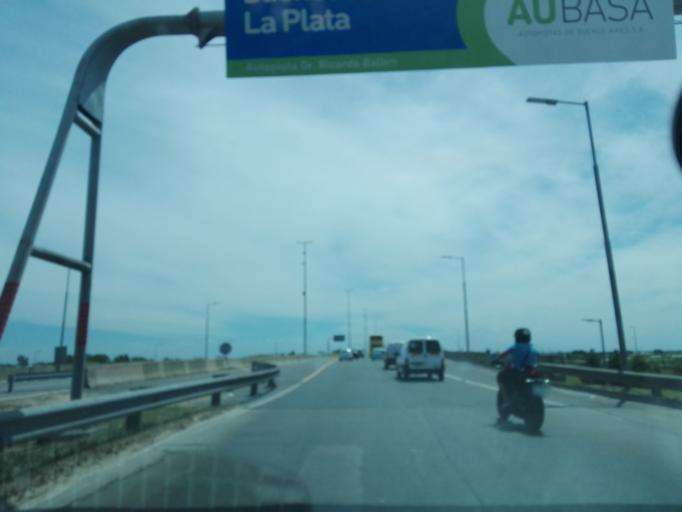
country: AR
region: Buenos Aires
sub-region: Partido de La Plata
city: La Plata
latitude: -34.8815
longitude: -57.9565
